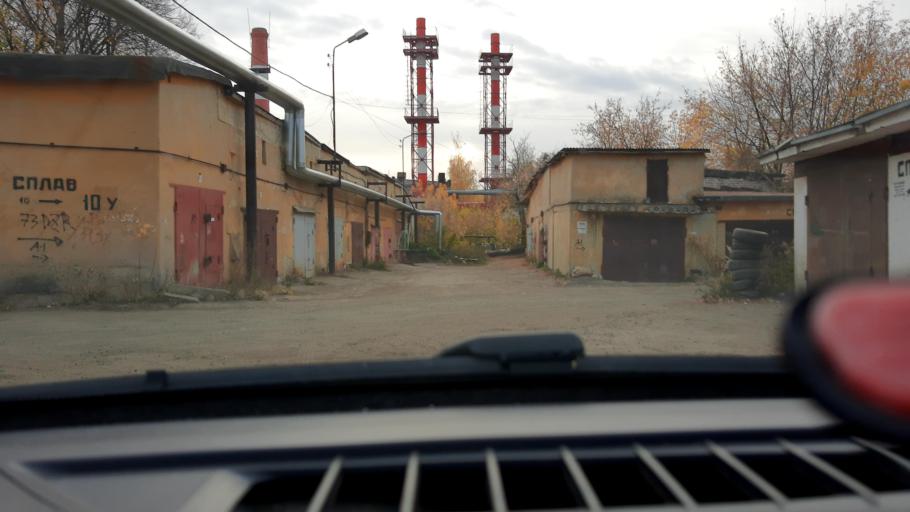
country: RU
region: Nizjnij Novgorod
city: Gorbatovka
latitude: 56.3270
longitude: 43.8476
